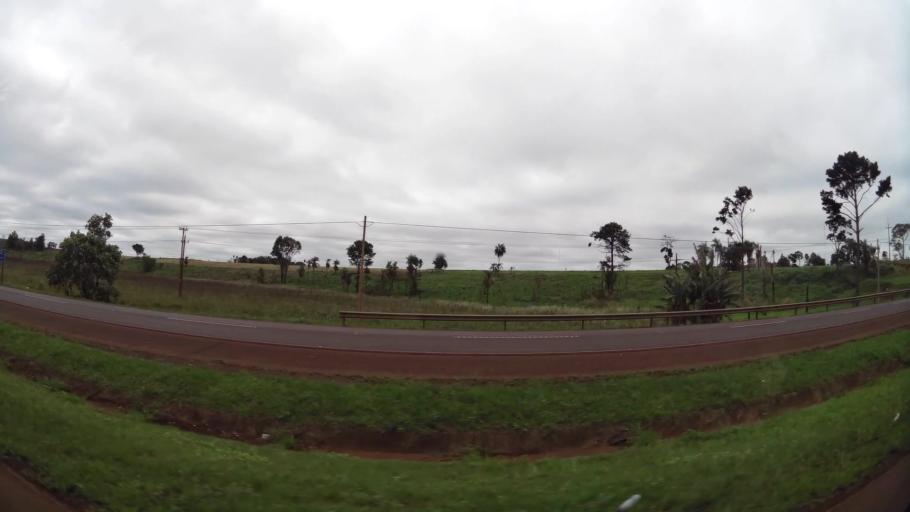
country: PY
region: Alto Parana
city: Colonia Yguazu
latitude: -25.4881
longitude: -54.8251
